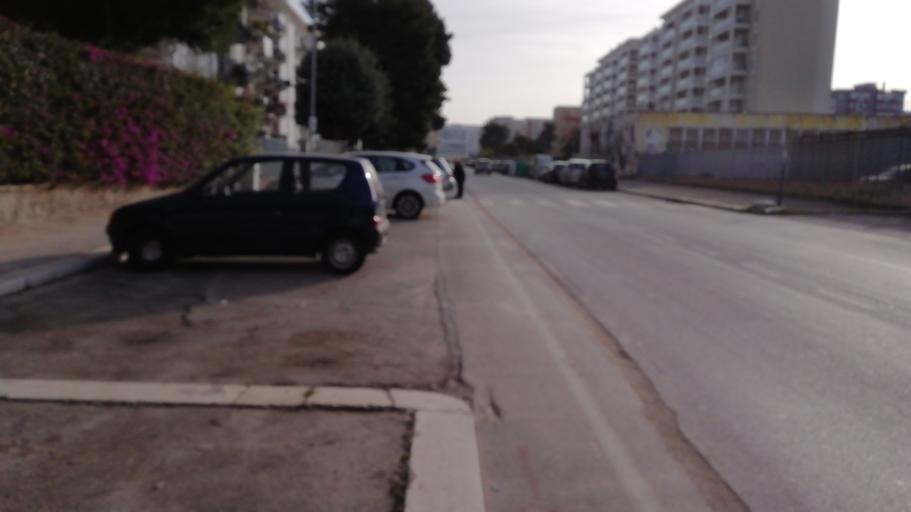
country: IT
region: Apulia
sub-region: Provincia di Bari
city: Triggiano
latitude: 41.1062
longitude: 16.9144
